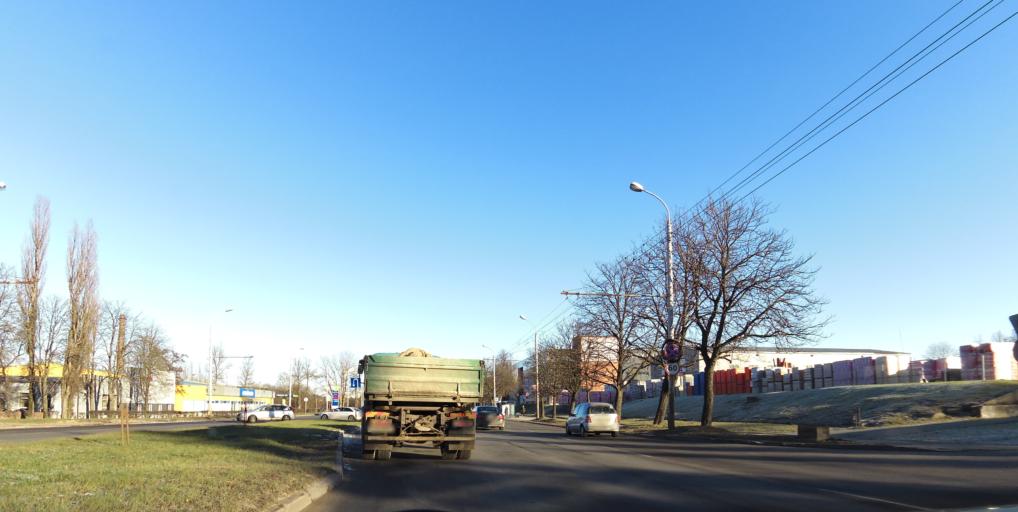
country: LT
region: Vilnius County
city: Lazdynai
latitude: 54.6468
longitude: 25.2112
